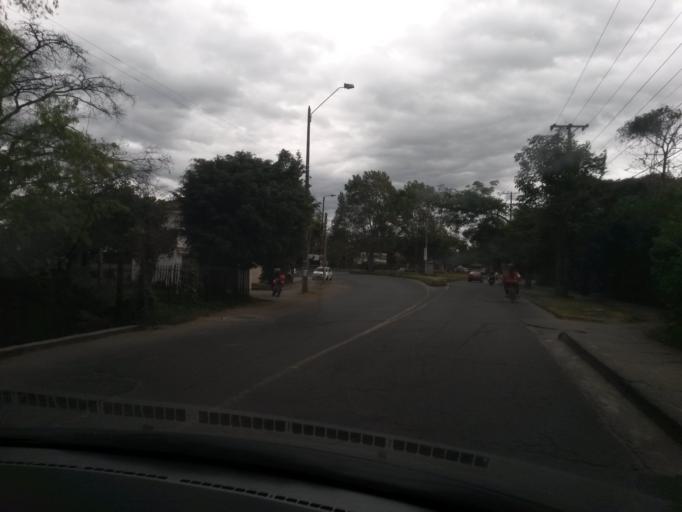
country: CO
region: Cauca
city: Popayan
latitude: 2.4591
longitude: -76.5987
